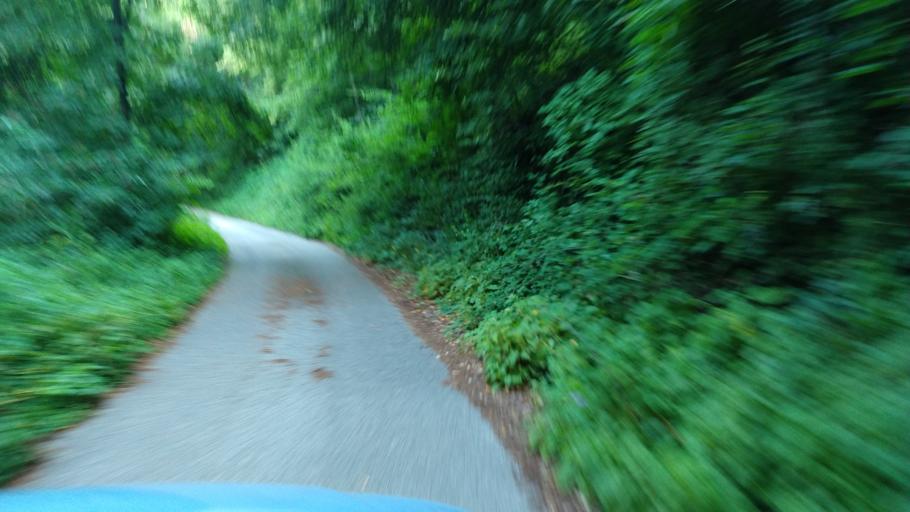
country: IT
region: Veneto
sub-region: Provincia di Vicenza
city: Campolongo sul Brenta
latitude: 45.8227
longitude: 11.6955
